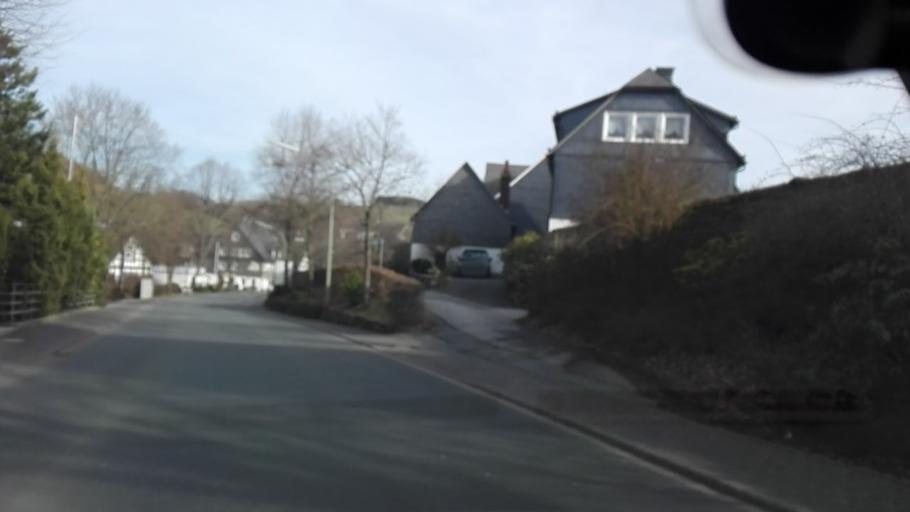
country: DE
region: North Rhine-Westphalia
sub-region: Regierungsbezirk Arnsberg
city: Schmallenberg
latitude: 51.1456
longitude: 8.3248
